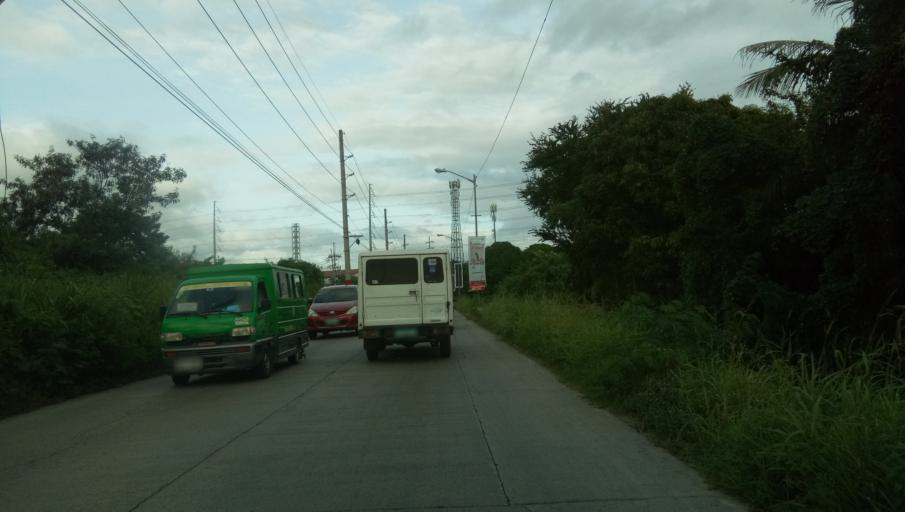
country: PH
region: Calabarzon
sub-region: Province of Cavite
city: Dasmarinas
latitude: 14.3693
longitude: 120.9361
